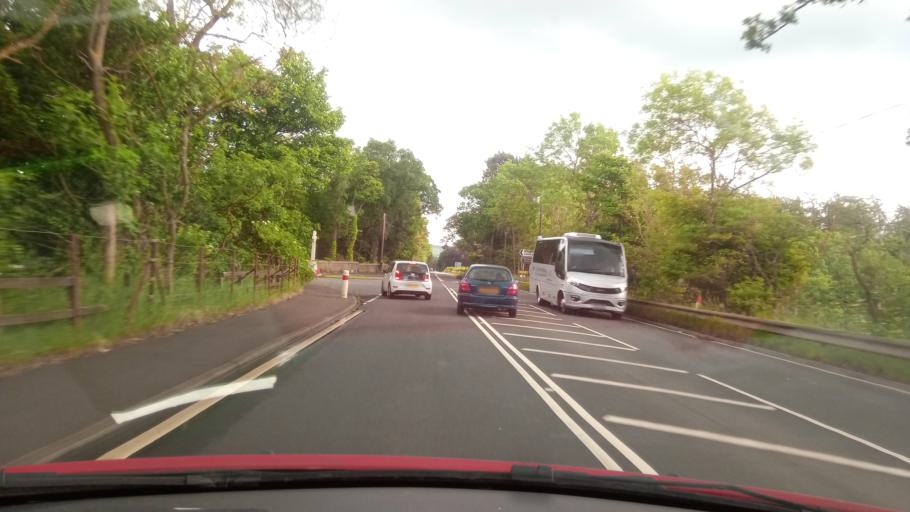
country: GB
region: Scotland
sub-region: Fife
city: Pathhead
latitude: 55.8846
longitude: -2.9915
